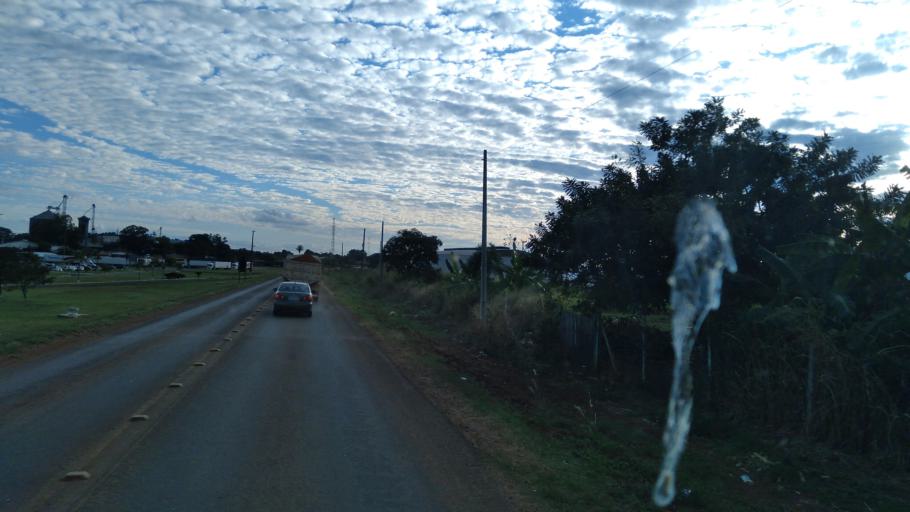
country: BR
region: Goias
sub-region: Mineiros
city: Mineiros
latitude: -17.5787
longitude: -52.5374
